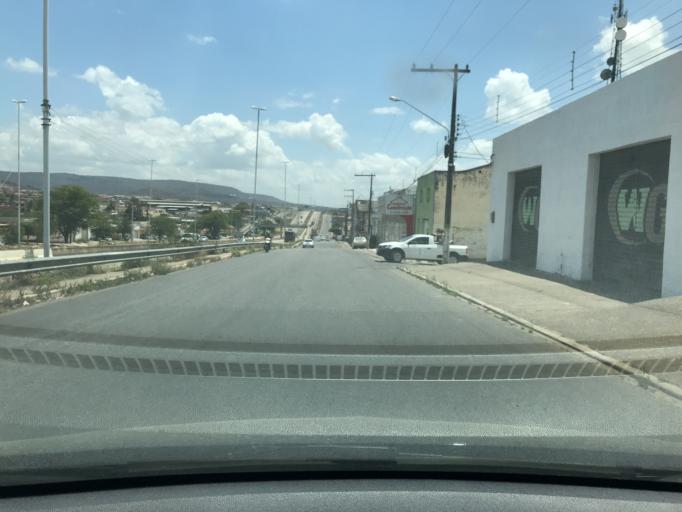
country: BR
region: Pernambuco
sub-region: Bezerros
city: Bezerros
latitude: -8.2429
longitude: -35.7526
